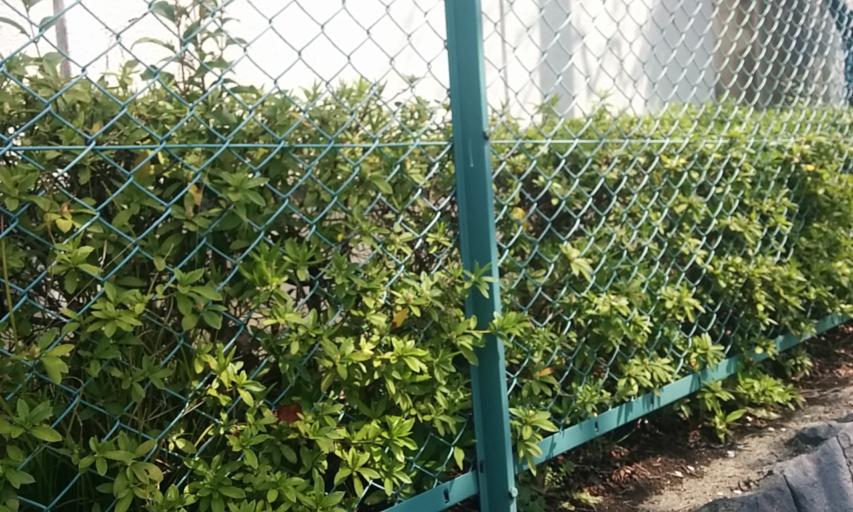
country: JP
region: Tokyo
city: Urayasu
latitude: 35.6849
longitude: 139.8603
